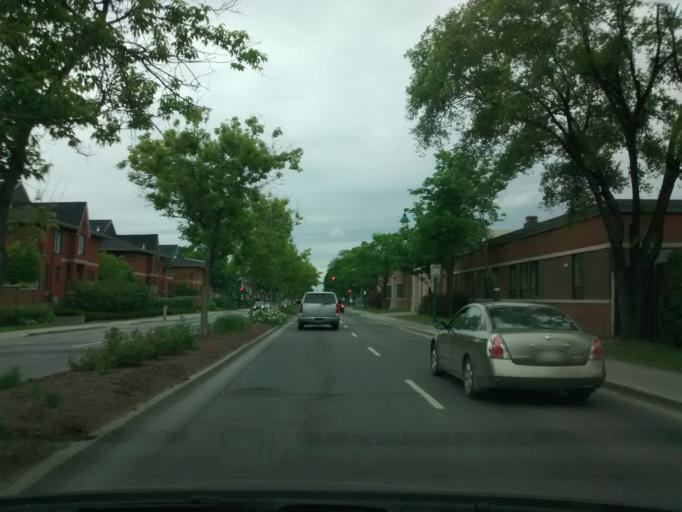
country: CA
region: Quebec
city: Mont-Royal
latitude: 45.5169
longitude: -73.6302
